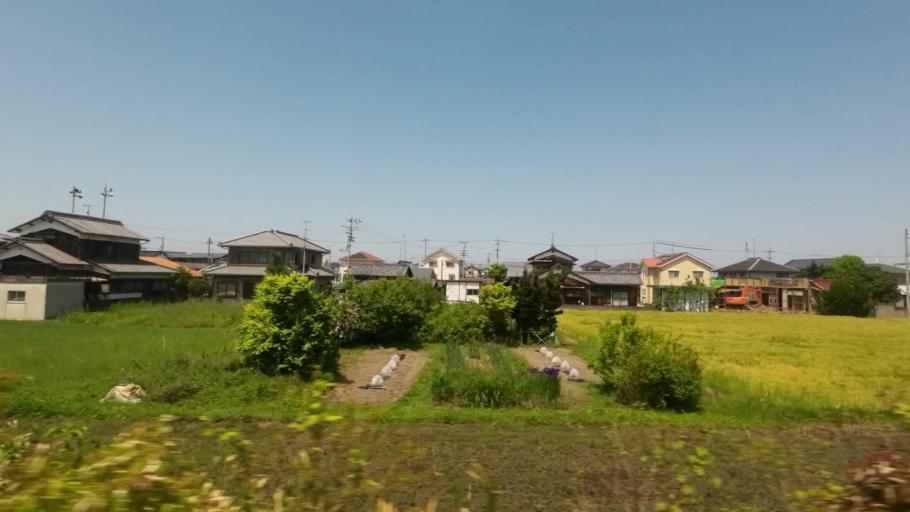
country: JP
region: Ehime
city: Hojo
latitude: 33.9391
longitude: 132.7688
